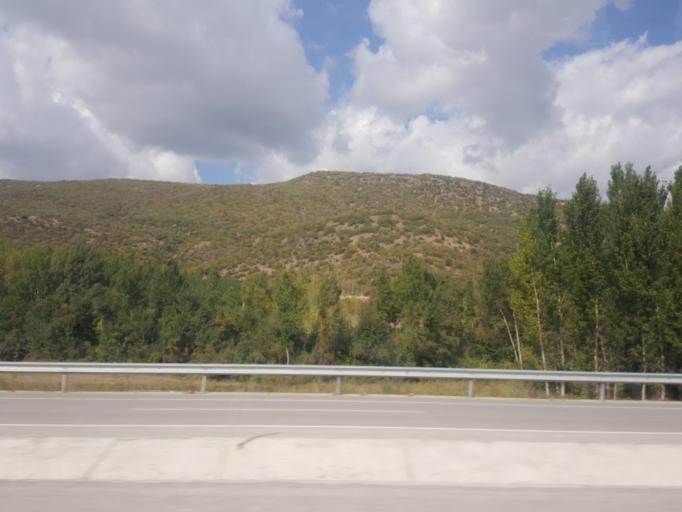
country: TR
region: Tokat
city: Gokdere
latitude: 40.3955
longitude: 36.7038
